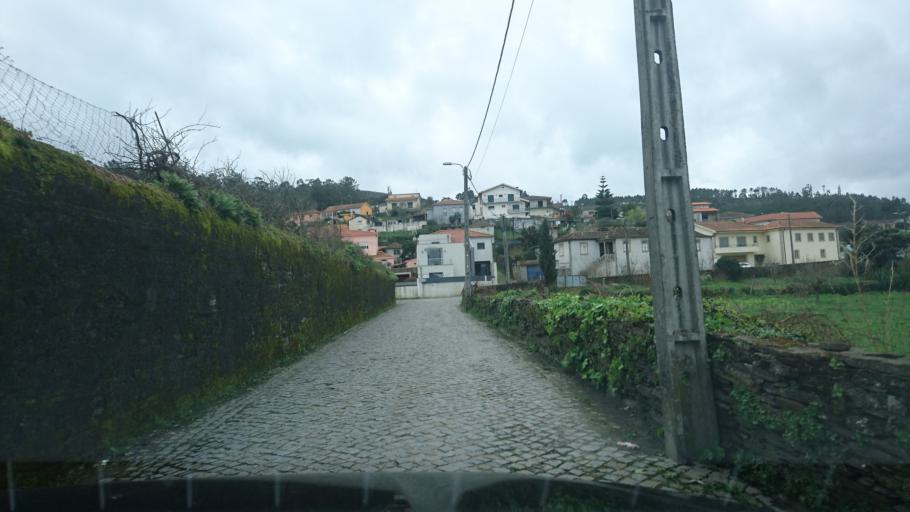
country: PT
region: Porto
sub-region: Paredes
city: Recarei
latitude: 41.1390
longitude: -8.3924
